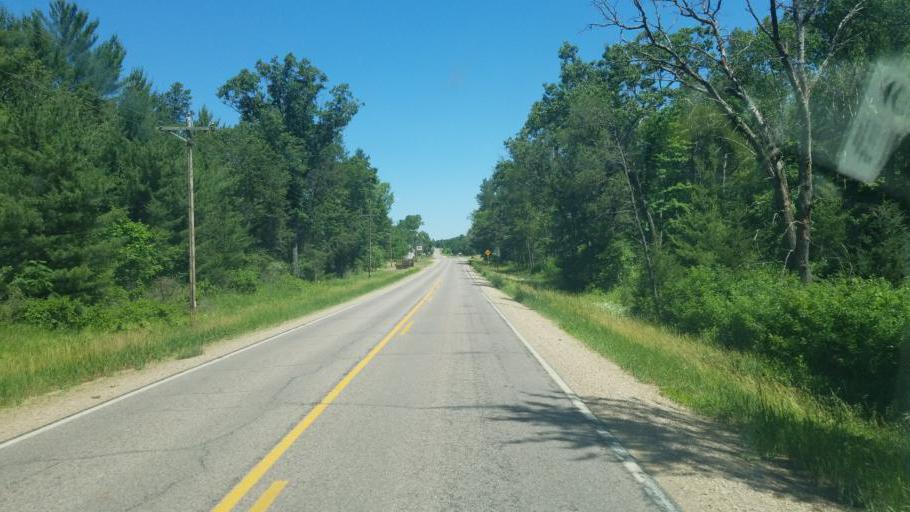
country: US
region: Wisconsin
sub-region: Adams County
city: Adams
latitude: 43.9601
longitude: -89.9376
